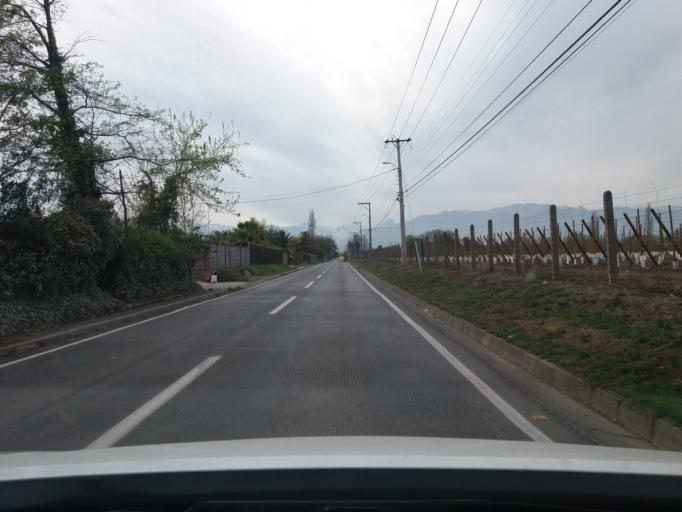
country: CL
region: Valparaiso
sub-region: Provincia de Los Andes
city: Los Andes
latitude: -32.8223
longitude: -70.6698
